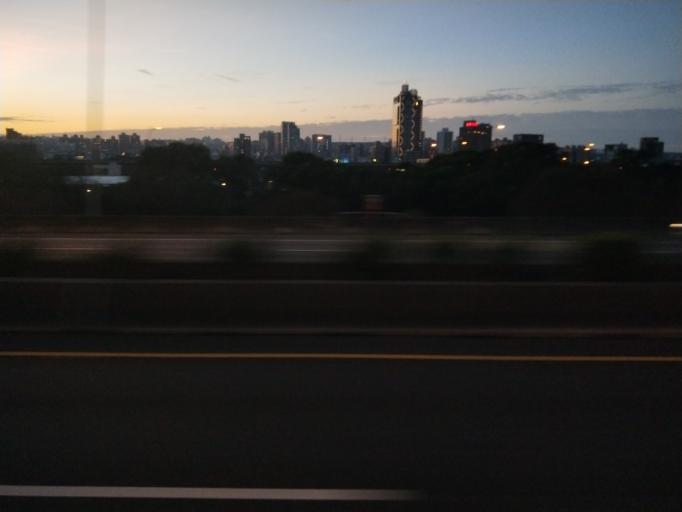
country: TW
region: Taiwan
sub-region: Taichung City
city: Taichung
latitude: 24.1739
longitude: 120.6300
